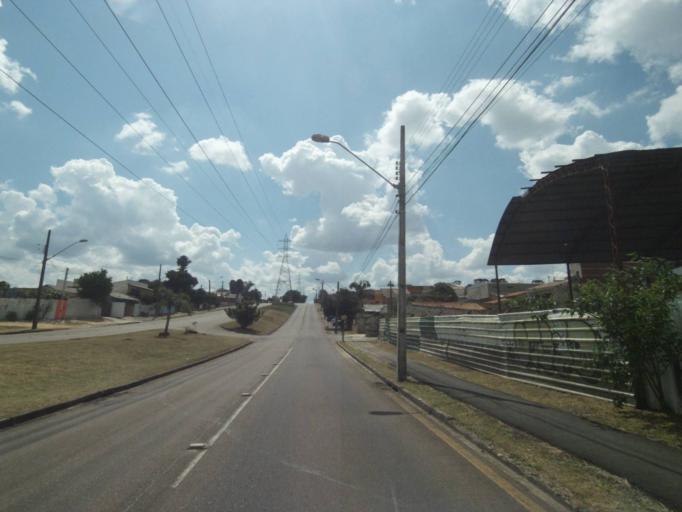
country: BR
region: Parana
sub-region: Sao Jose Dos Pinhais
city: Sao Jose dos Pinhais
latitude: -25.5343
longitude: -49.2830
